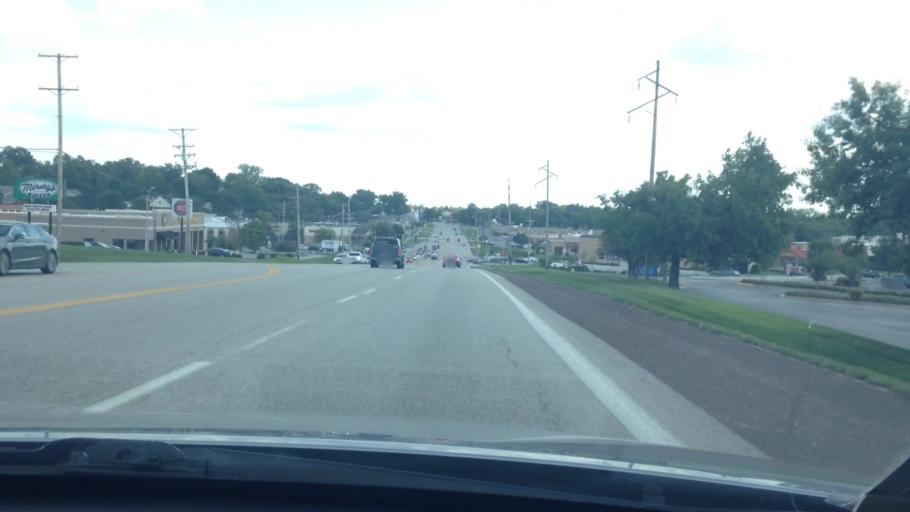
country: US
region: Missouri
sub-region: Clay County
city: Liberty
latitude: 39.2467
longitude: -94.4453
